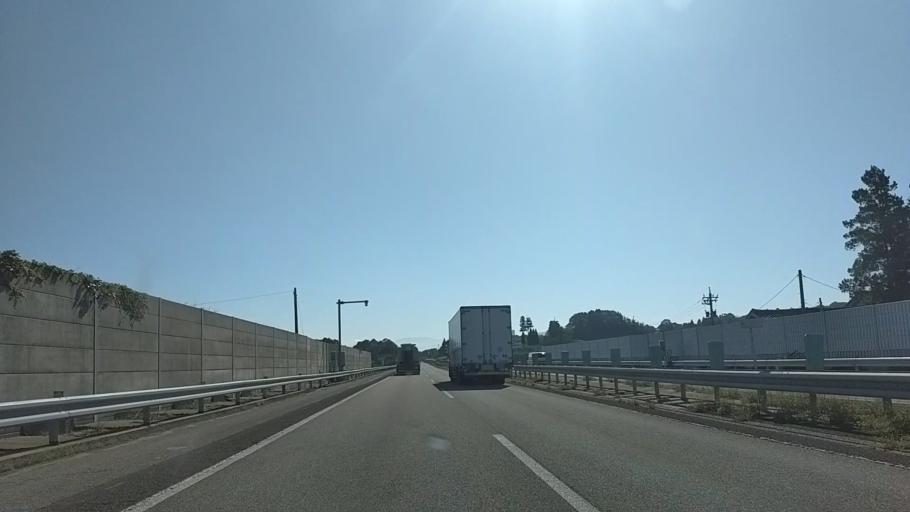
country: JP
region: Toyama
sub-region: Oyabe Shi
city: Oyabe
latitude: 36.6290
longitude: 136.8579
